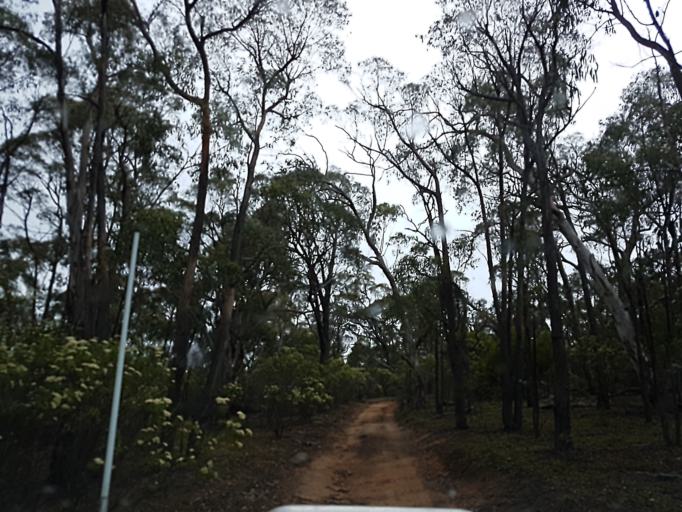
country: AU
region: New South Wales
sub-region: Snowy River
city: Jindabyne
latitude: -36.8835
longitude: 148.3385
